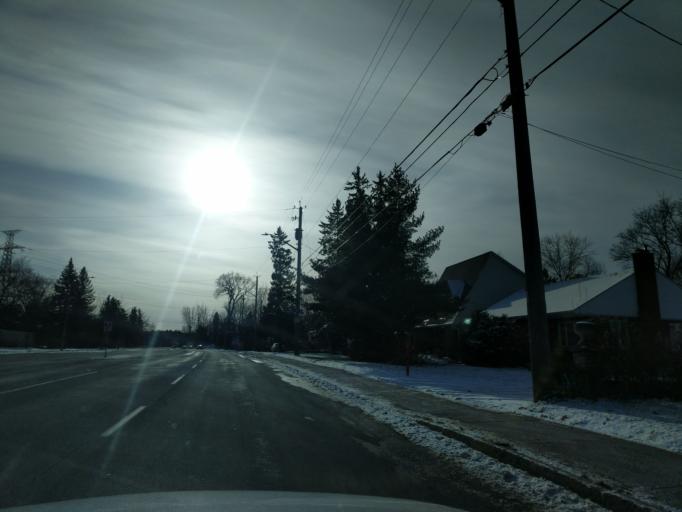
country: CA
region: Ontario
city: Ottawa
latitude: 45.3556
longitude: -75.6916
